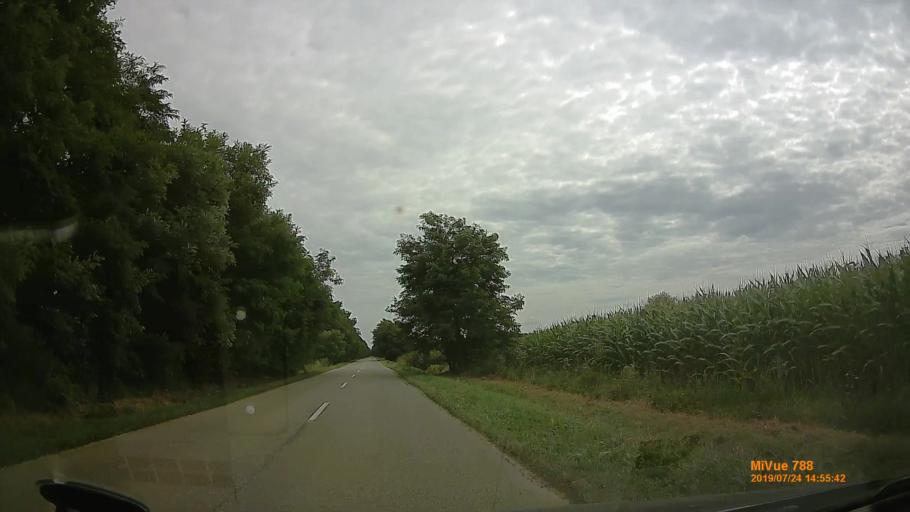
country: HU
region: Szabolcs-Szatmar-Bereg
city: Aranyosapati
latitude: 48.2531
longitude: 22.3149
